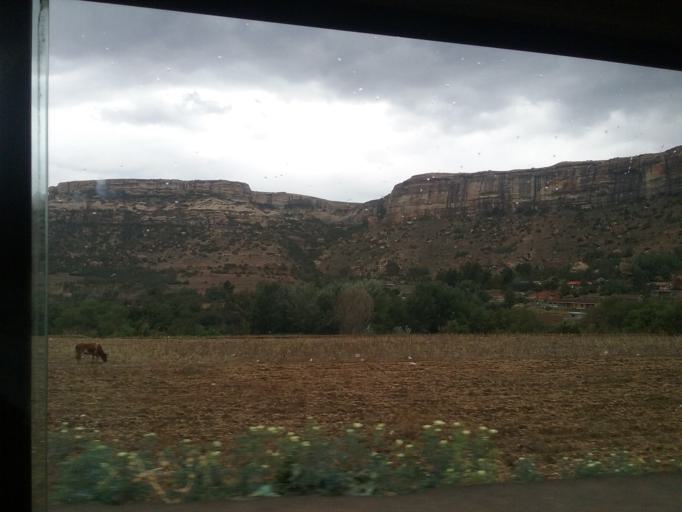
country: LS
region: Maseru
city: Nako
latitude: -29.4711
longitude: 27.7391
